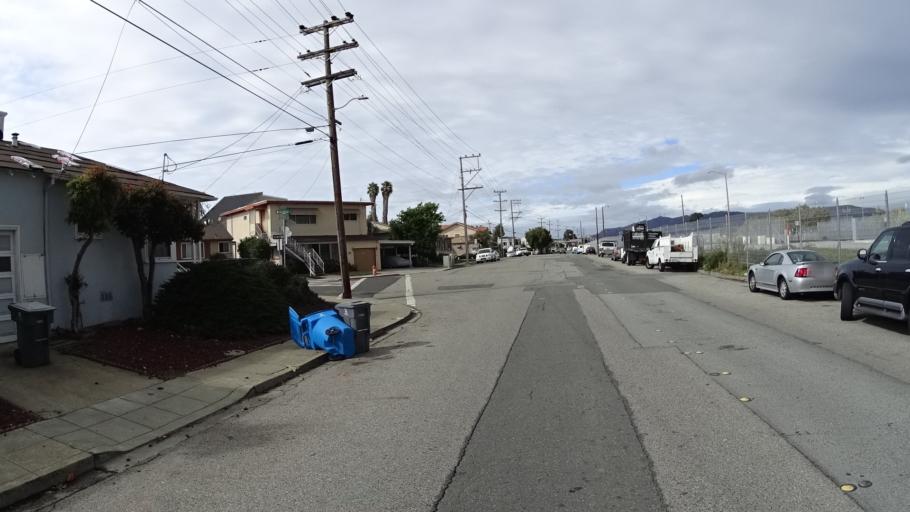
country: US
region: California
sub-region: San Mateo County
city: San Bruno
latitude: 37.6212
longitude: -122.4065
